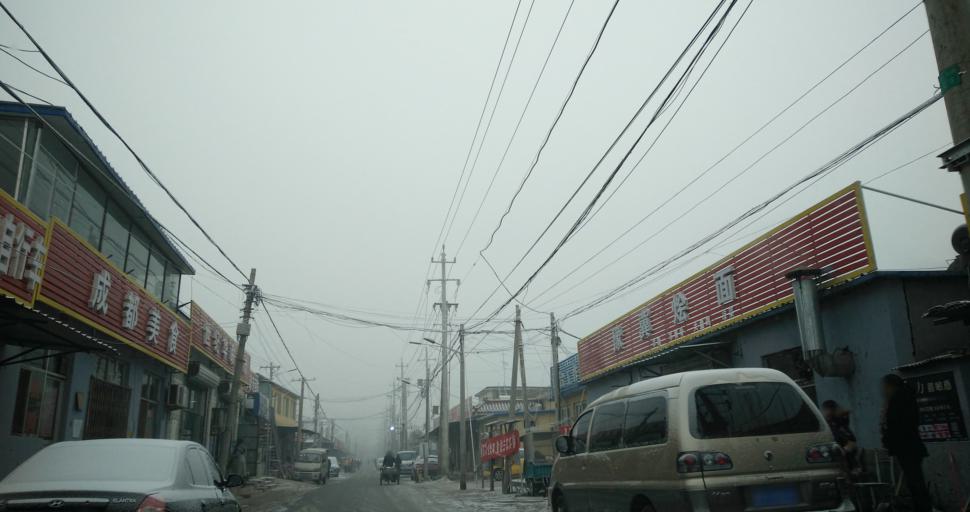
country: CN
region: Beijing
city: Yinghai
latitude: 39.7180
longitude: 116.4273
